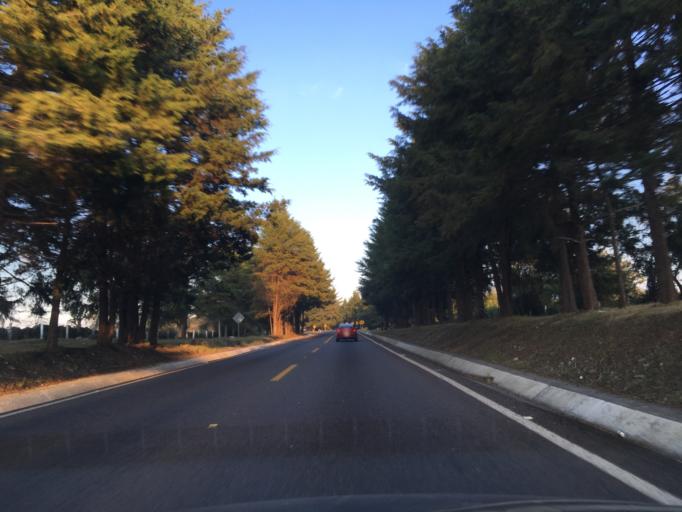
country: MX
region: Michoacan
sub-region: Patzcuaro
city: Santa Ana Chapitiro
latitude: 19.5129
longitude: -101.6705
